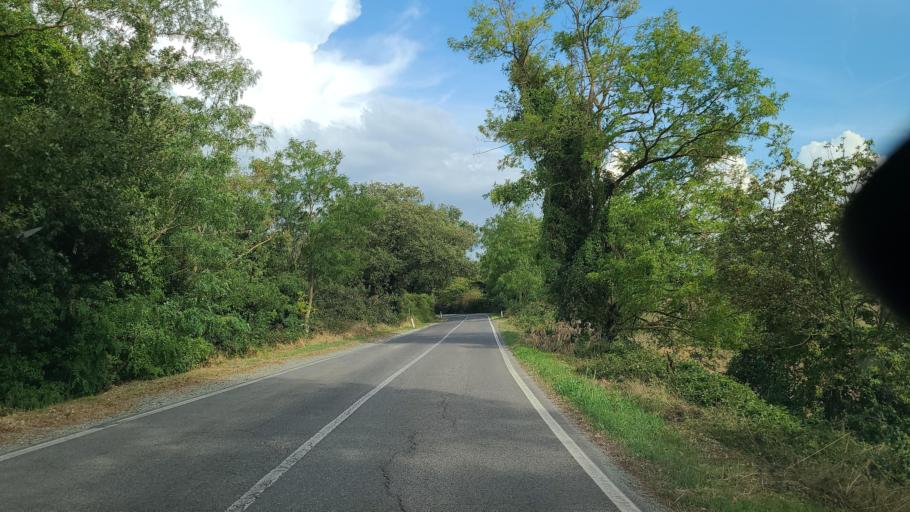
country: IT
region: Tuscany
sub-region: Provincia di Siena
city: San Gimignano
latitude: 43.4872
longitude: 10.9786
